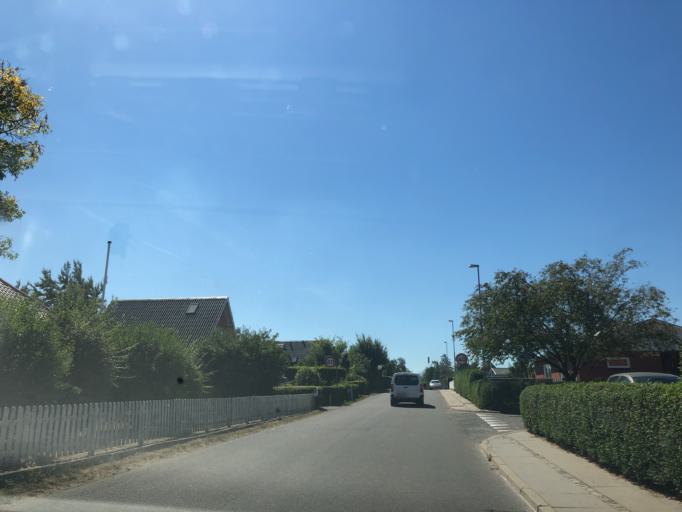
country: DK
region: Zealand
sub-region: Slagelse Kommune
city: Forlev
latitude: 55.3688
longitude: 11.2603
